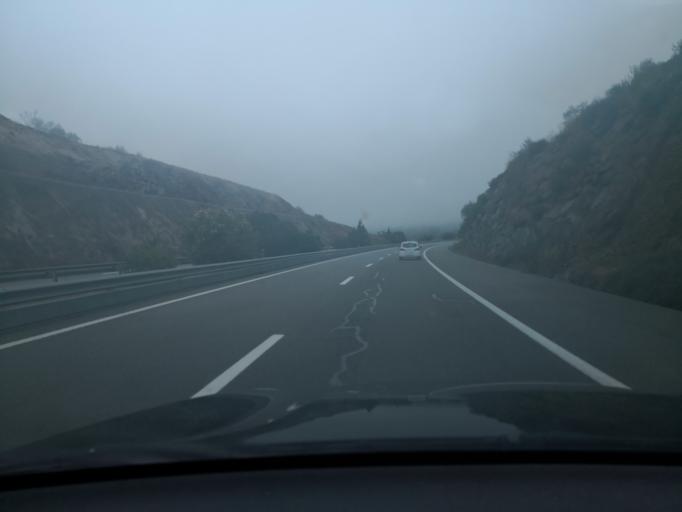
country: PT
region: Braga
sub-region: Celorico de Basto
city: Celorico de Basto
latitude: 41.4482
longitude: -8.0678
